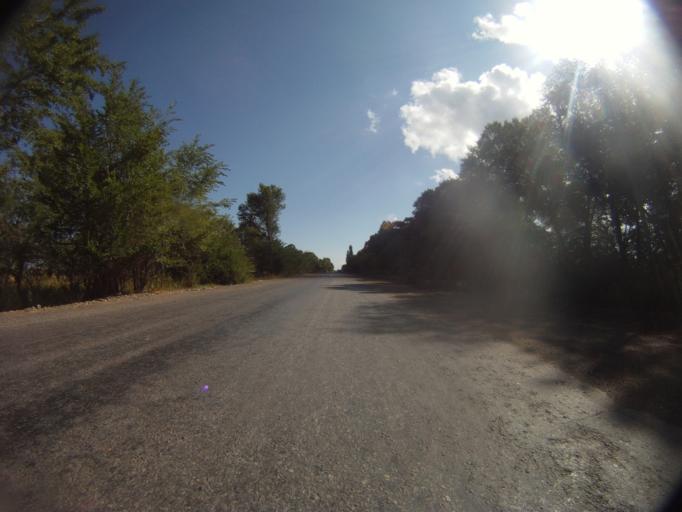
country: KG
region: Ysyk-Koel
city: Balykchy
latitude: 42.3144
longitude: 76.3235
